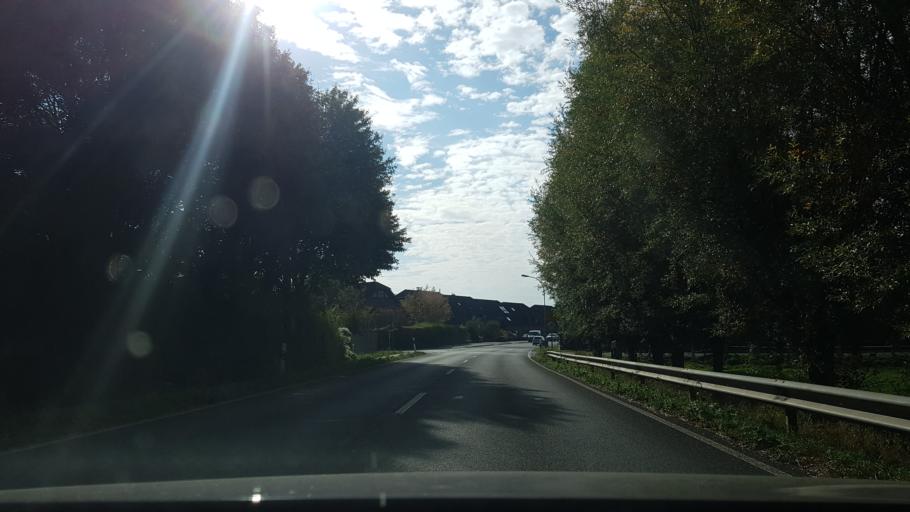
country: DE
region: North Rhine-Westphalia
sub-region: Regierungsbezirk Dusseldorf
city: Moers
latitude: 51.4267
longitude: 6.6159
